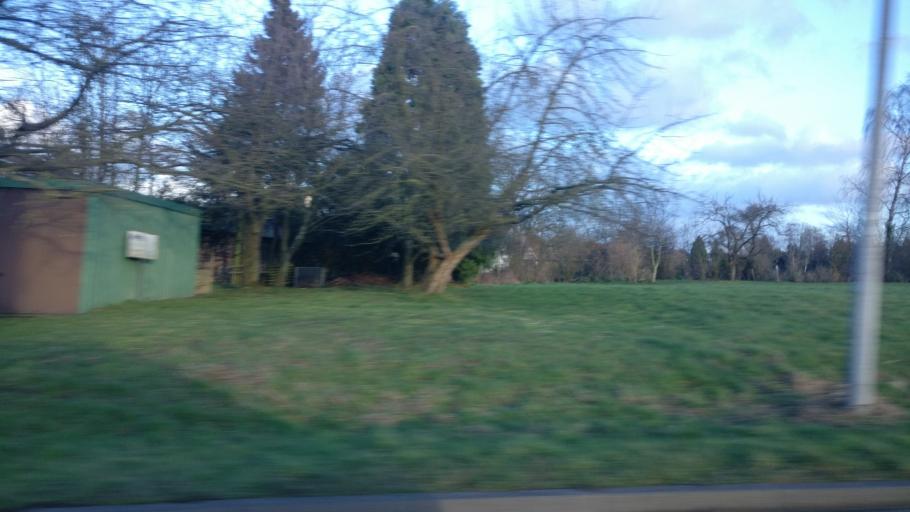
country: DE
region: North Rhine-Westphalia
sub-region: Regierungsbezirk Detmold
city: Lage
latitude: 52.0129
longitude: 8.7929
